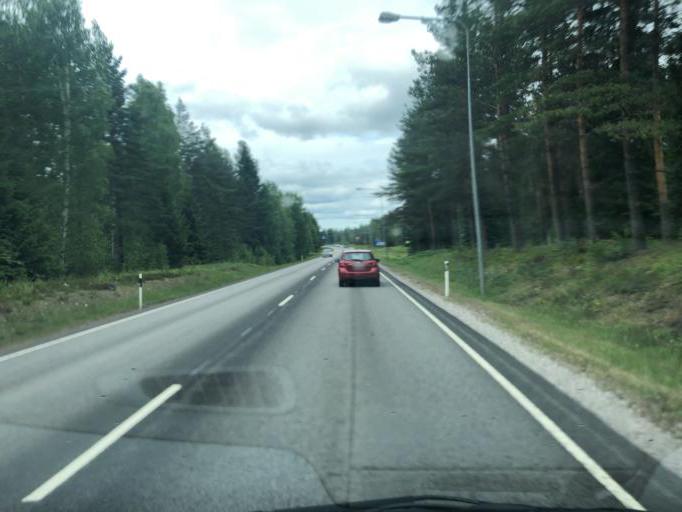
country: FI
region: Kymenlaakso
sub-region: Kouvola
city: Kouvola
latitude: 60.9170
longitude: 26.7793
